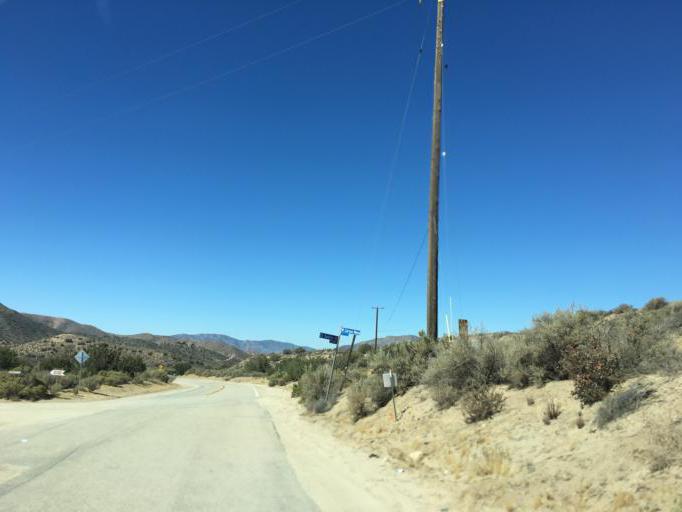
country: US
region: California
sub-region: Los Angeles County
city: Vincent
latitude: 34.4826
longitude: -118.1405
